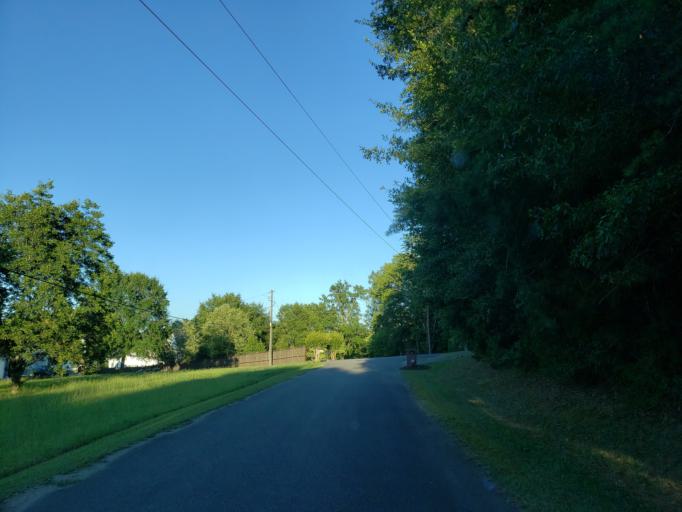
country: US
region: Georgia
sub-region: Bartow County
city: Euharlee
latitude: 34.0965
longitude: -84.9674
